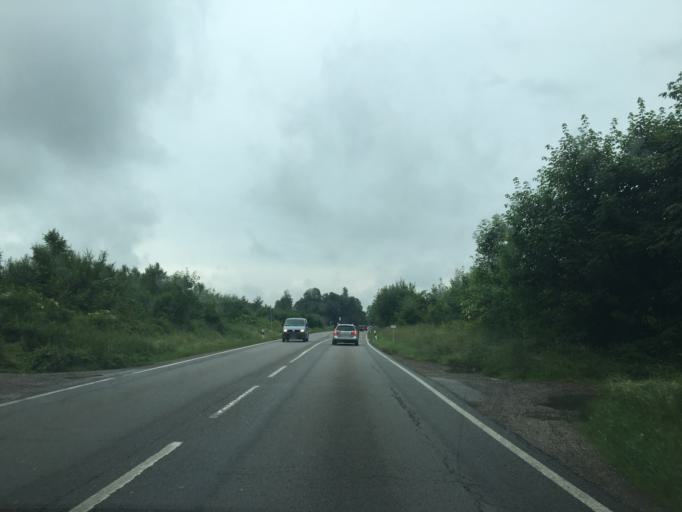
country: DE
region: Bavaria
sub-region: Upper Bavaria
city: Holzkirchen
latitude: 47.8887
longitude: 11.7231
